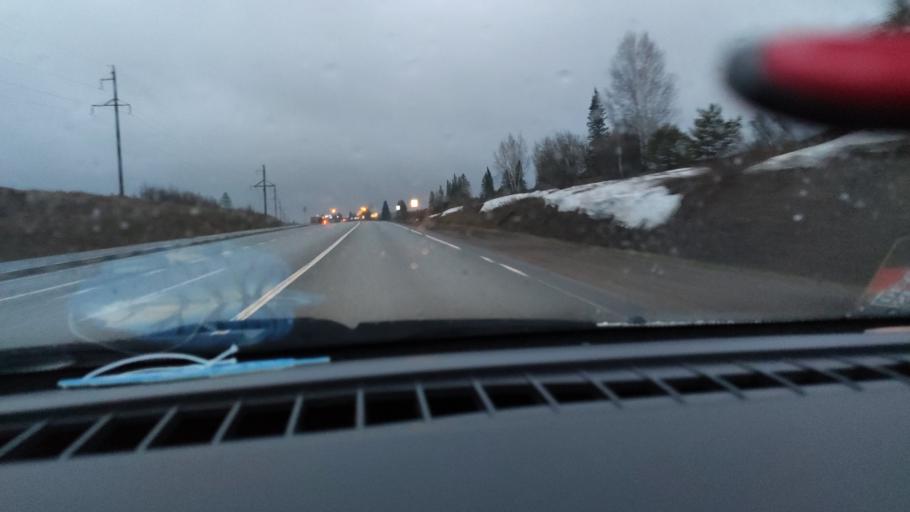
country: RU
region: Udmurtiya
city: Alnashi
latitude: 56.2569
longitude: 52.3765
